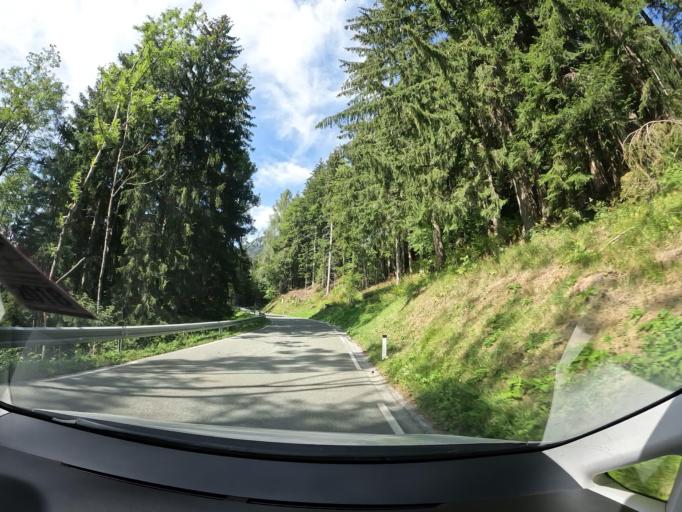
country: AT
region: Carinthia
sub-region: Politischer Bezirk Feldkirchen
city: Glanegg
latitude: 46.7344
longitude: 14.2142
